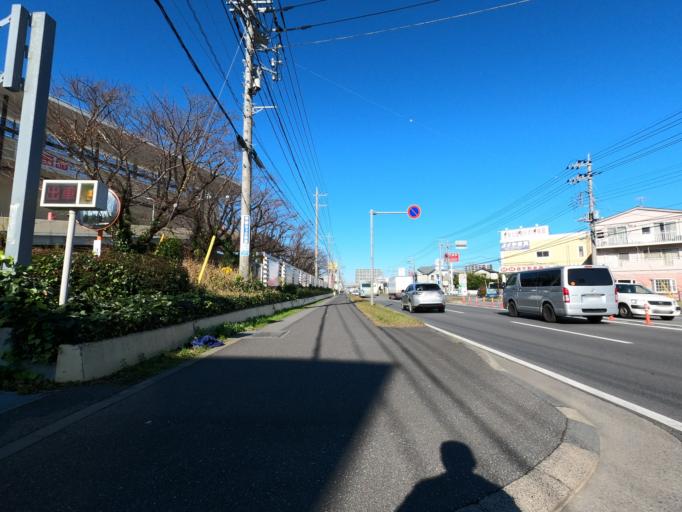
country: JP
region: Ibaraki
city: Moriya
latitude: 35.9445
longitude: 139.9929
